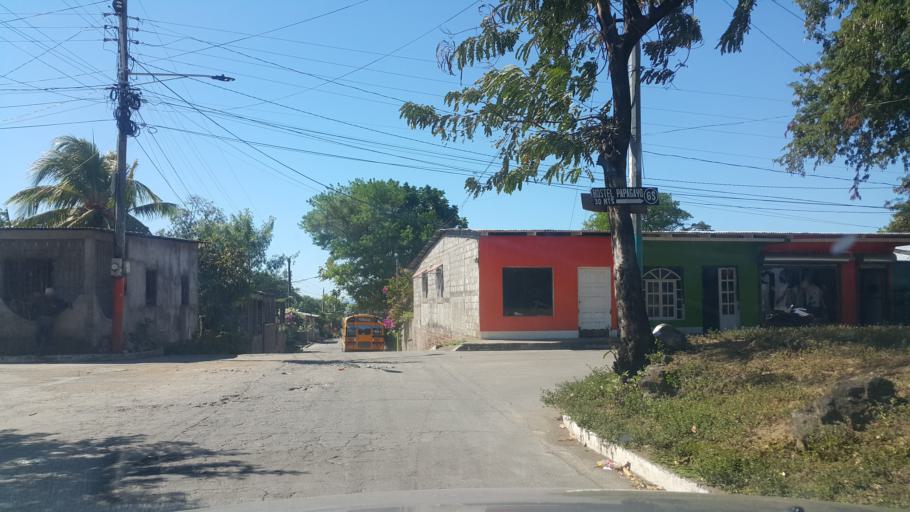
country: NI
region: Rivas
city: Moyogalpa
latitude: 11.5396
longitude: -85.6988
